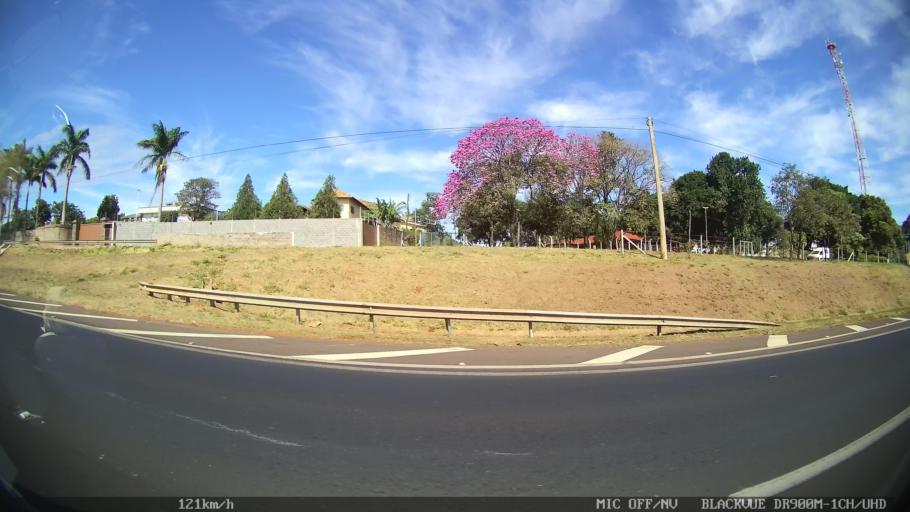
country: BR
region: Sao Paulo
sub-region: Sao Jose Do Rio Preto
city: Sao Jose do Rio Preto
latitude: -20.8154
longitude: -49.4614
